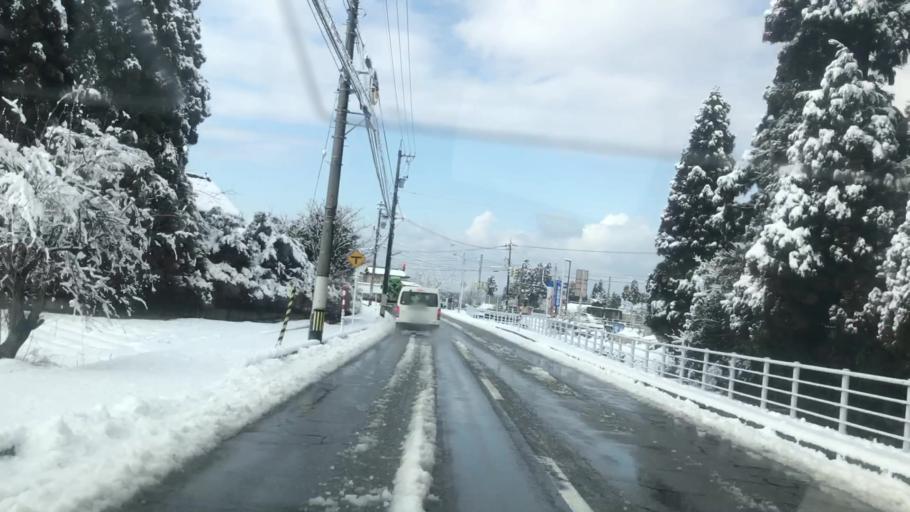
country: JP
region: Toyama
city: Toyama-shi
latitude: 36.6291
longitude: 137.2367
